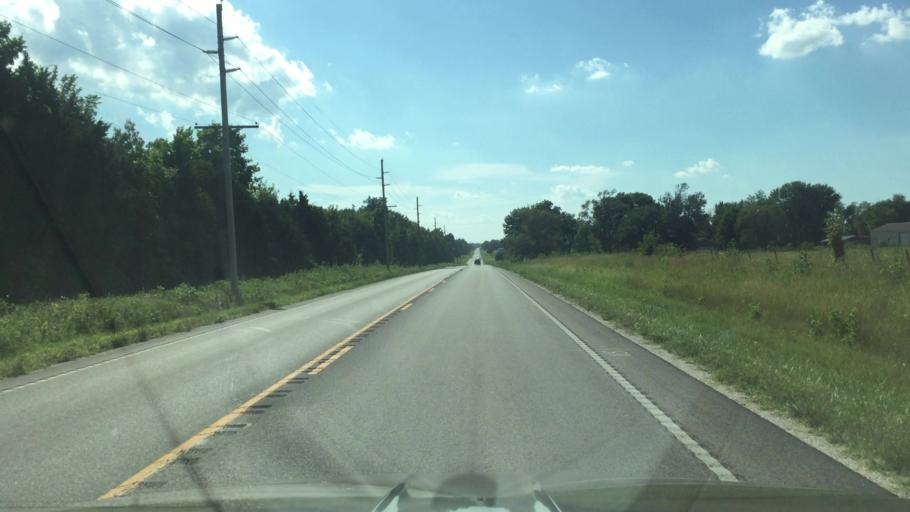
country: US
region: Missouri
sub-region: Morgan County
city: Versailles
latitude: 38.3938
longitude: -92.7140
